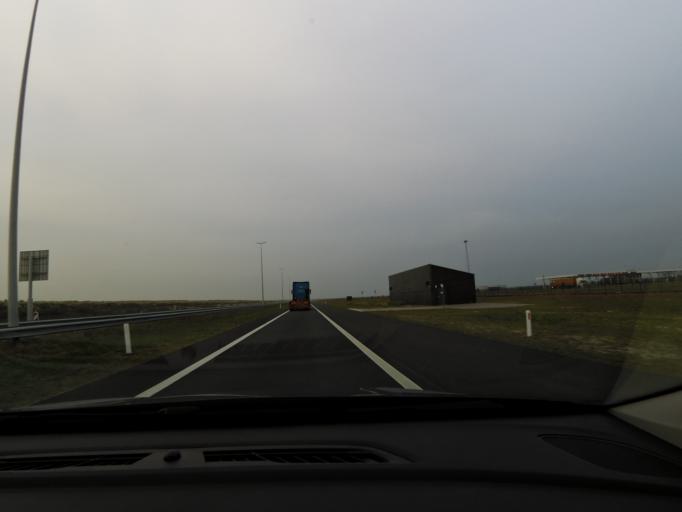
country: NL
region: South Holland
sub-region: Gemeente Goeree-Overflakkee
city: Goedereede
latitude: 51.9418
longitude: 3.9736
